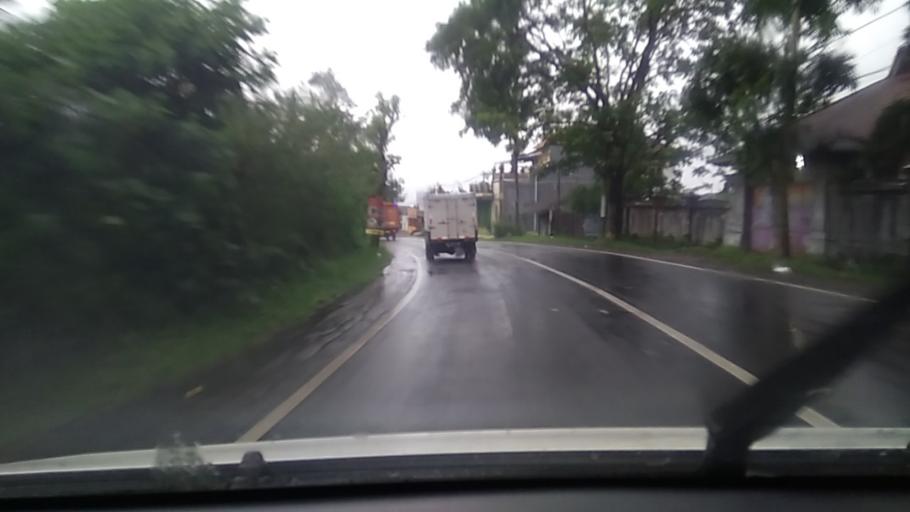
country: ID
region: Bali
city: Peneng
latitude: -8.3035
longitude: 115.1758
